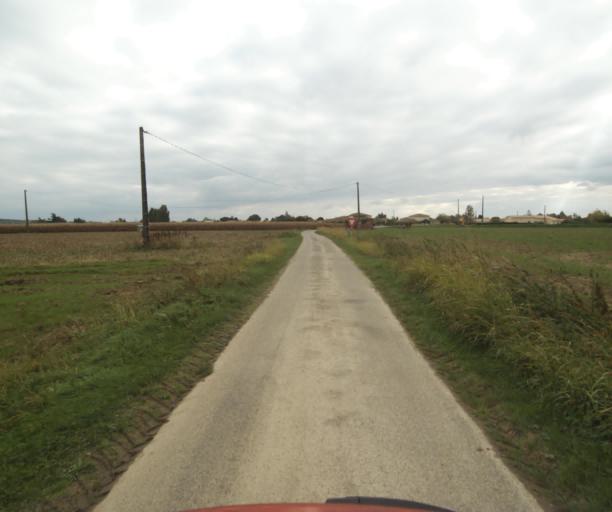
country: FR
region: Midi-Pyrenees
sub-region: Departement du Tarn-et-Garonne
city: Verdun-sur-Garonne
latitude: 43.8877
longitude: 1.2497
